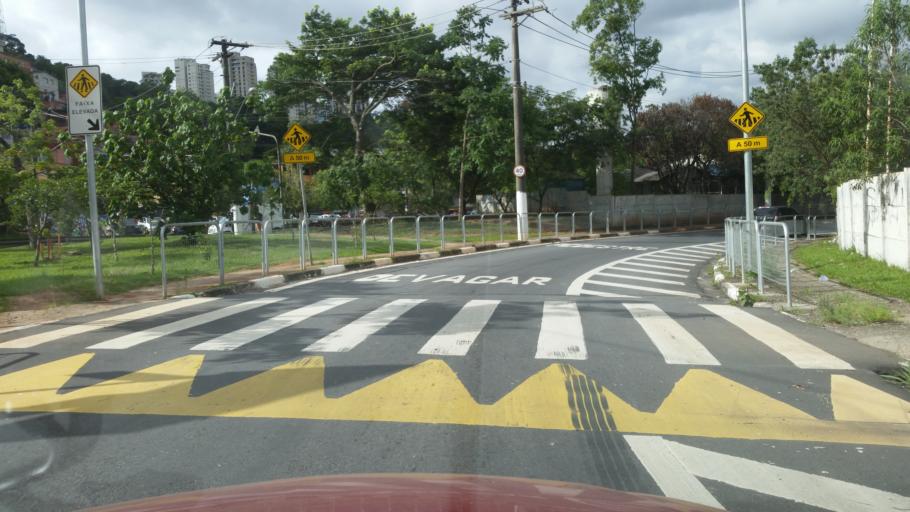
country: BR
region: Sao Paulo
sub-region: Taboao Da Serra
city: Taboao da Serra
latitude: -23.6438
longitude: -46.7285
